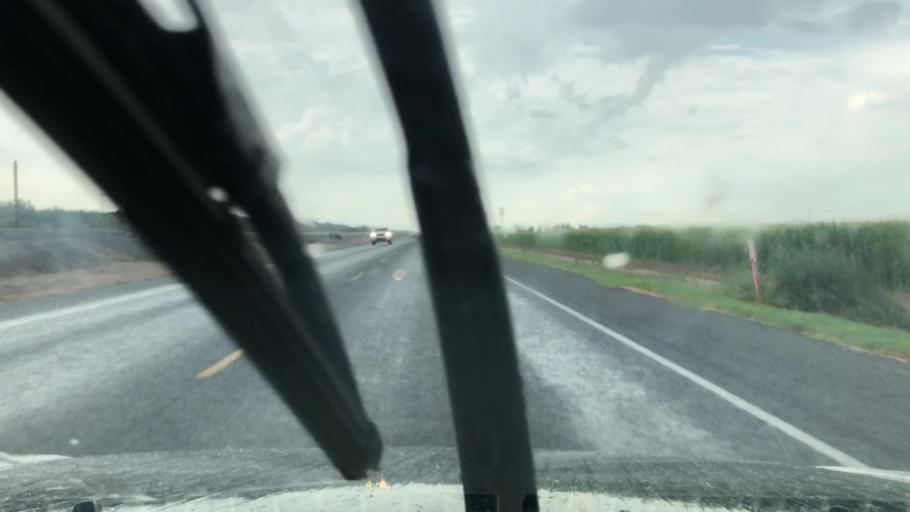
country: US
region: New Mexico
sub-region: Dona Ana County
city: Mesquite
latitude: 32.1453
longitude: -106.6844
